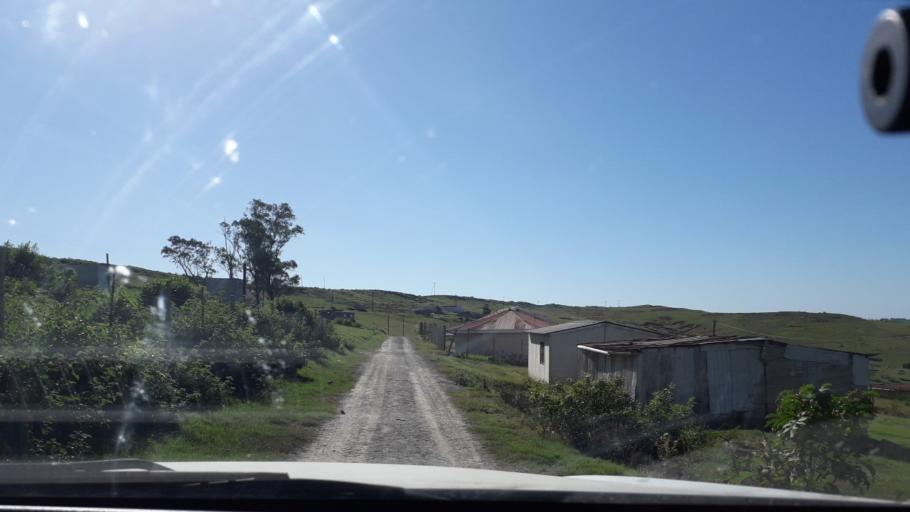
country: ZA
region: Eastern Cape
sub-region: Buffalo City Metropolitan Municipality
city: East London
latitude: -32.8427
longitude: 27.9924
